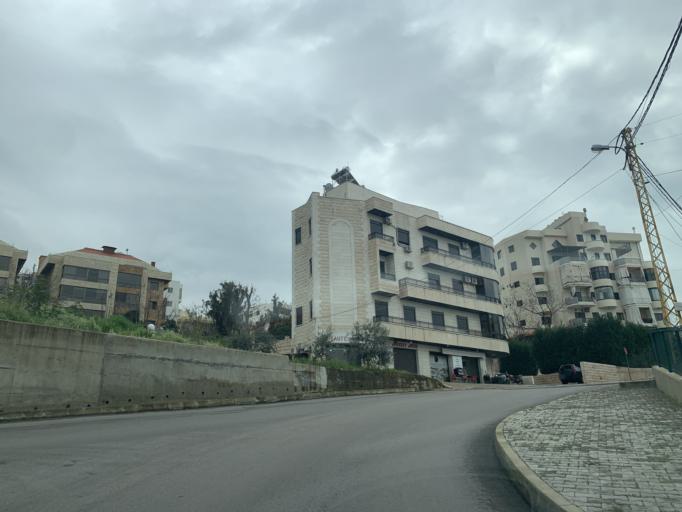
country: LB
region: Mont-Liban
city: Djounie
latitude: 34.0463
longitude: 35.6367
